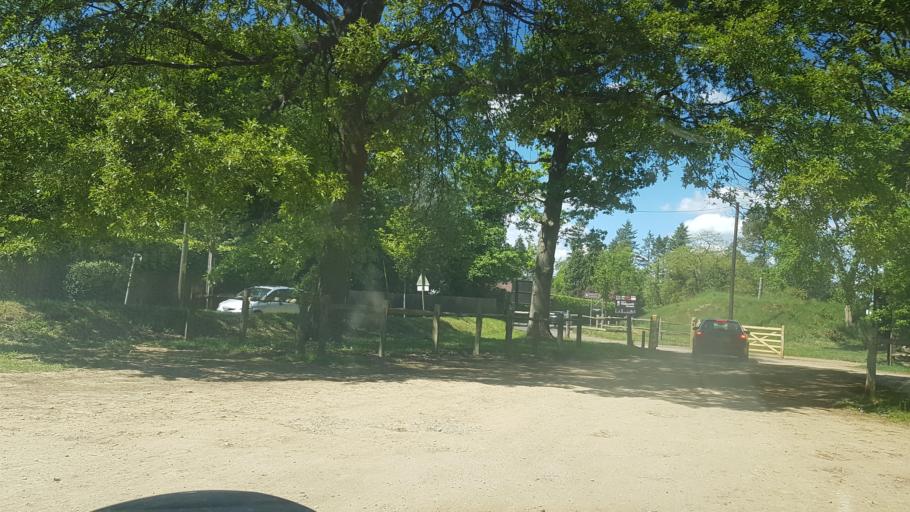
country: GB
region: England
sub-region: Surrey
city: Godalming
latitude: 51.1614
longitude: -0.5861
